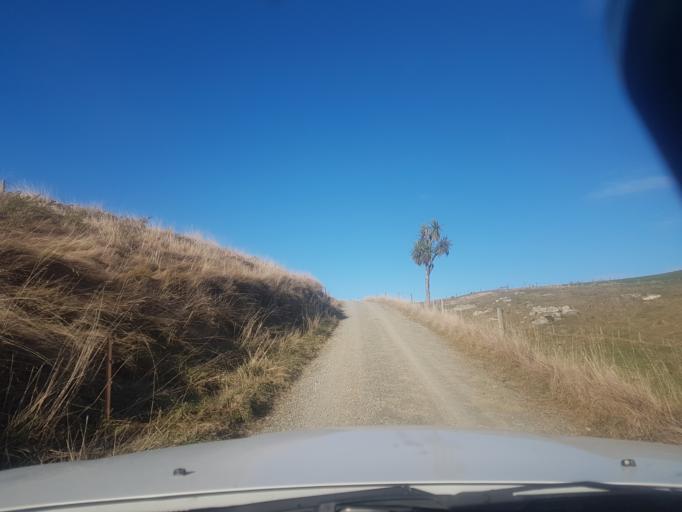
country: NZ
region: Canterbury
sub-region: Timaru District
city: Pleasant Point
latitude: -44.1766
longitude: 170.8889
